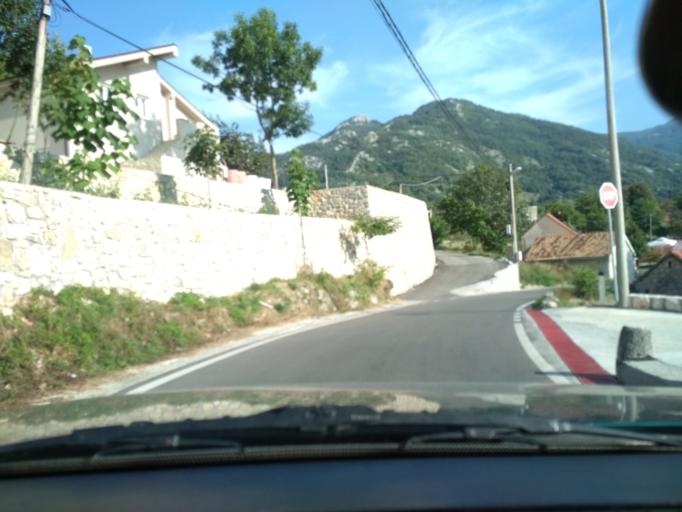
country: ME
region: Kotor
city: Kotor
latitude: 42.4369
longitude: 18.8296
